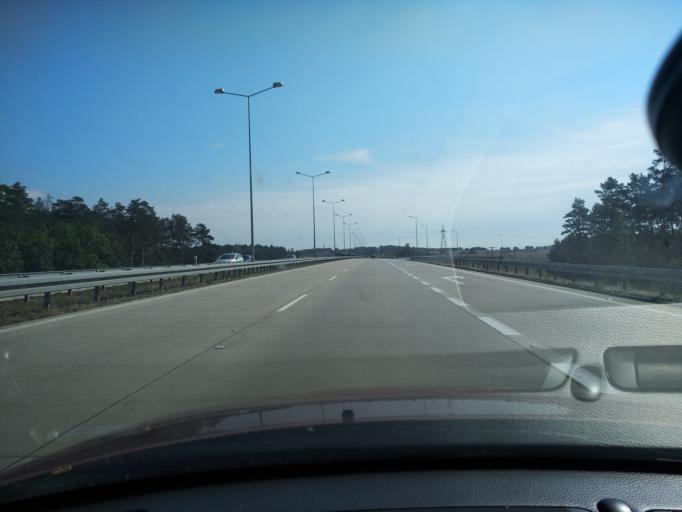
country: PL
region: Lower Silesian Voivodeship
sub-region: Powiat zgorzelecki
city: Wegliniec
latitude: 51.2167
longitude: 15.2380
